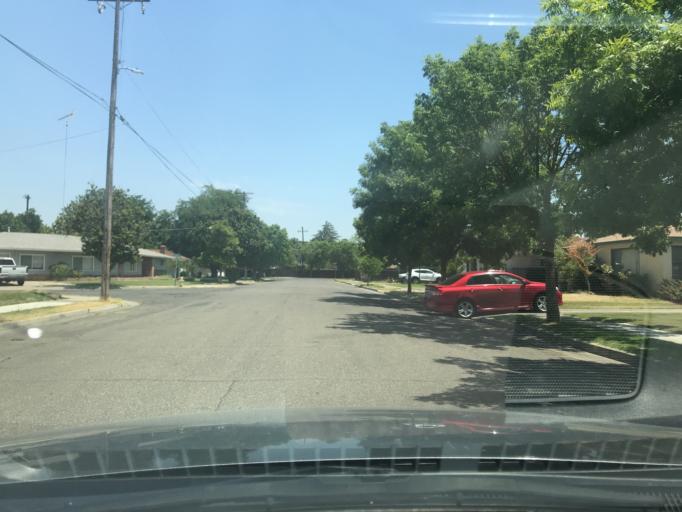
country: US
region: California
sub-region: Merced County
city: Atwater
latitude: 37.3559
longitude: -120.6052
